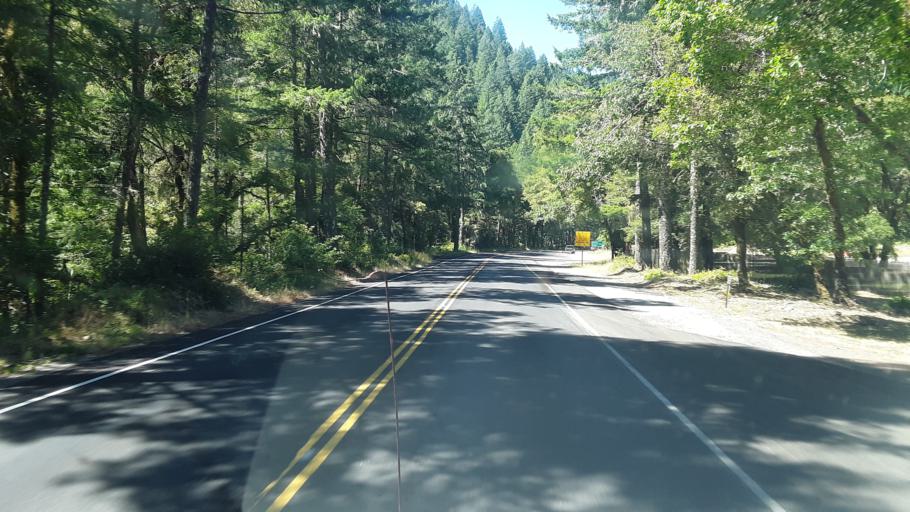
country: US
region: Oregon
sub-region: Josephine County
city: Cave Junction
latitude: 41.8992
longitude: -123.7700
